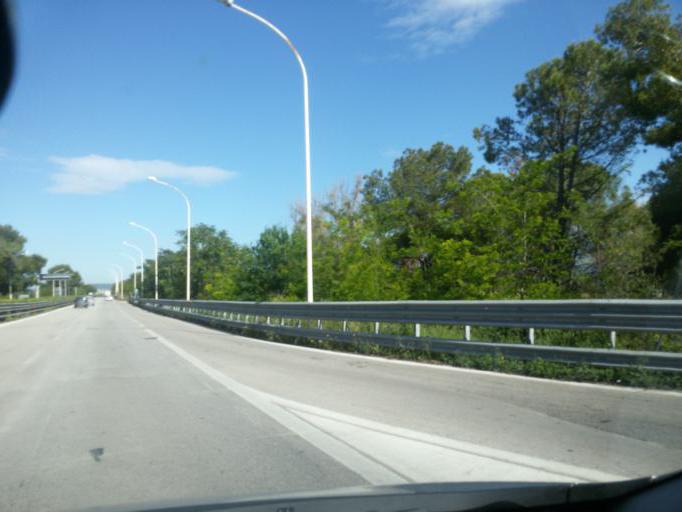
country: IT
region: Apulia
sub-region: Provincia di Taranto
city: Grottaglie
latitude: 40.5261
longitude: 17.4212
